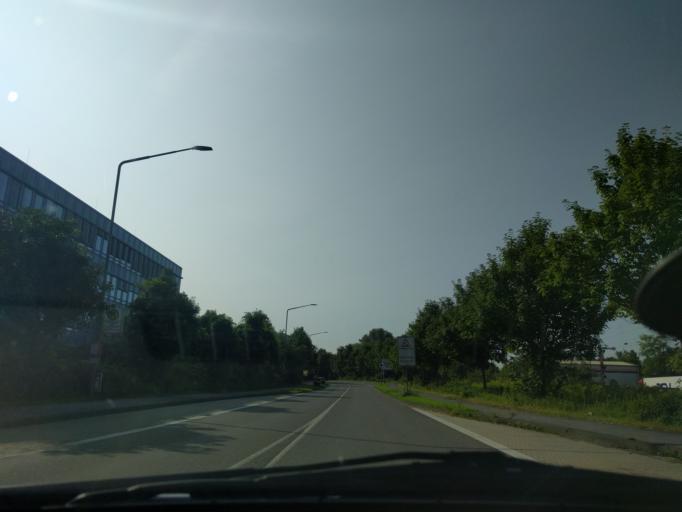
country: DE
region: North Rhine-Westphalia
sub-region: Regierungsbezirk Dusseldorf
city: Ratingen
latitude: 51.3029
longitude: 6.8388
